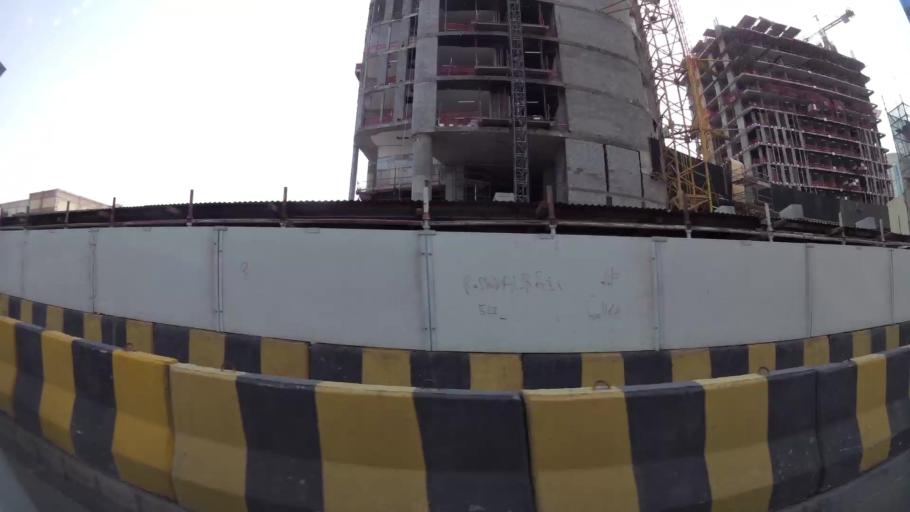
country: AE
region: Abu Dhabi
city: Abu Dhabi
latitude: 24.4721
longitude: 54.3512
